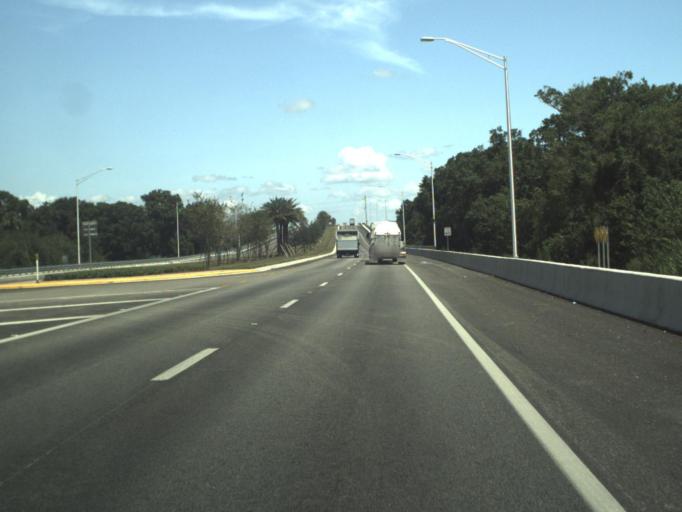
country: US
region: Florida
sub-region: Martin County
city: Indiantown
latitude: 27.0161
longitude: -80.4603
